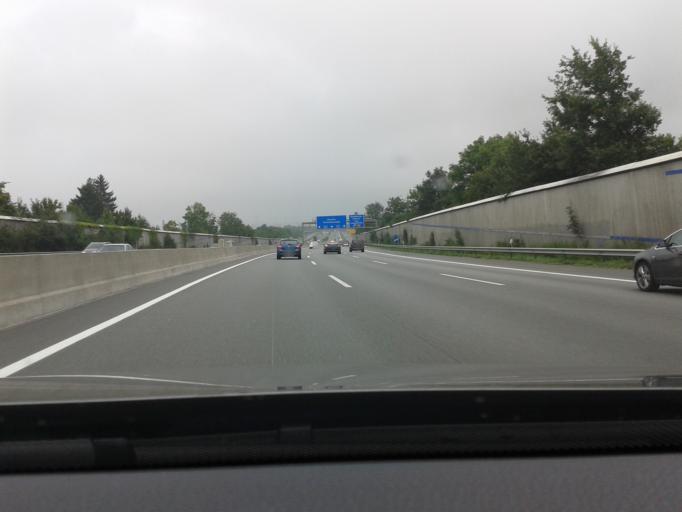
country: DE
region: North Rhine-Westphalia
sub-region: Regierungsbezirk Detmold
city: Oerlinghausen
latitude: 51.9876
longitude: 8.6153
